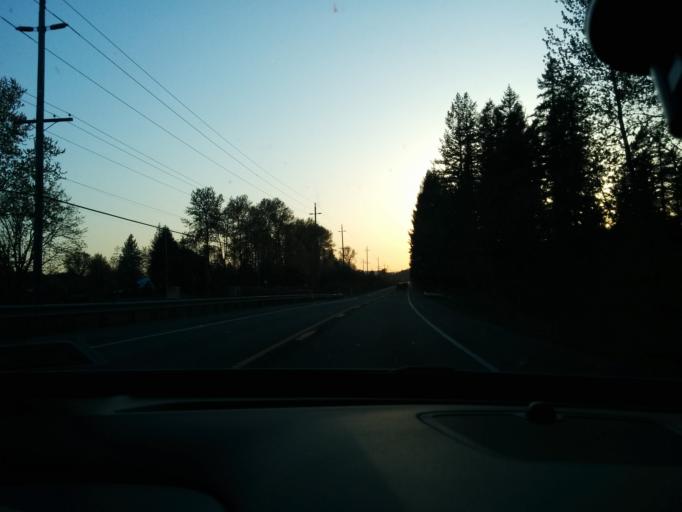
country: US
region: Washington
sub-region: Snohomish County
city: Woods Creek
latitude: 47.8548
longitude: -121.9060
